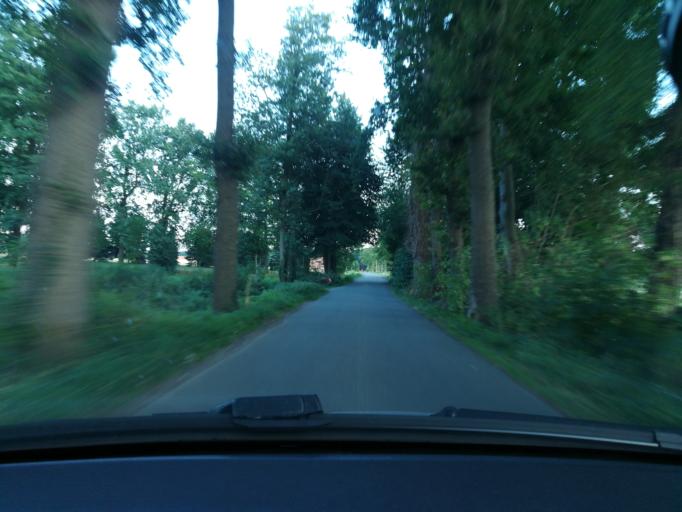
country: DE
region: North Rhine-Westphalia
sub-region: Regierungsbezirk Munster
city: Lienen
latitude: 52.1405
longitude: 7.9896
